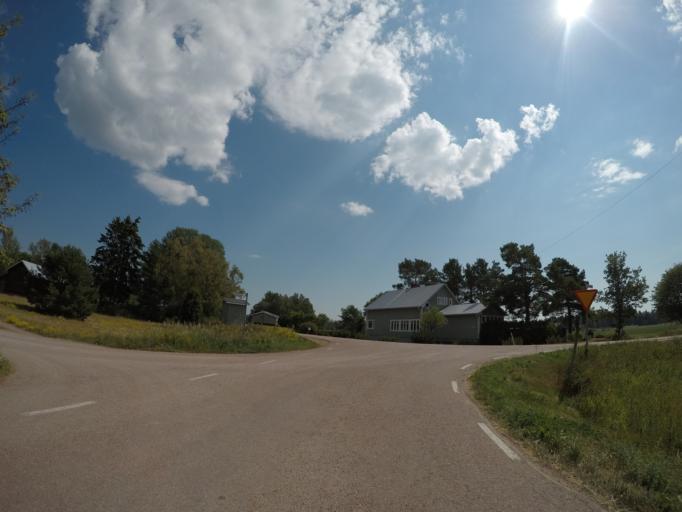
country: AX
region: Alands landsbygd
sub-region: Finstroem
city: Finstroem
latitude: 60.2495
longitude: 19.8798
